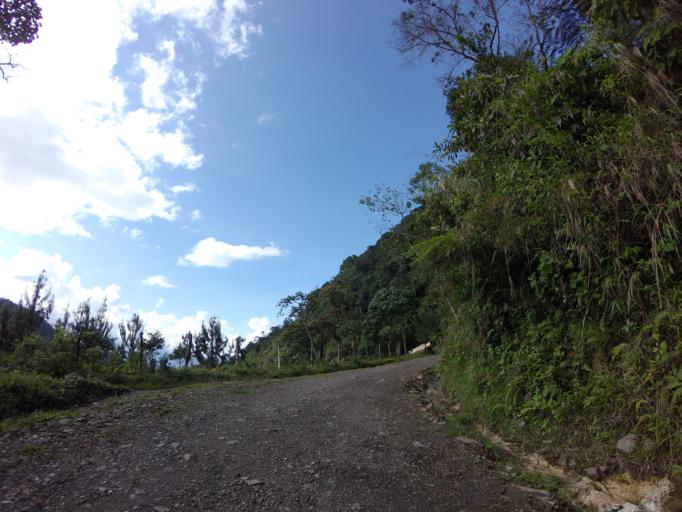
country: CO
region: Caldas
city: Pensilvania
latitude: 5.4539
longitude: -75.1517
